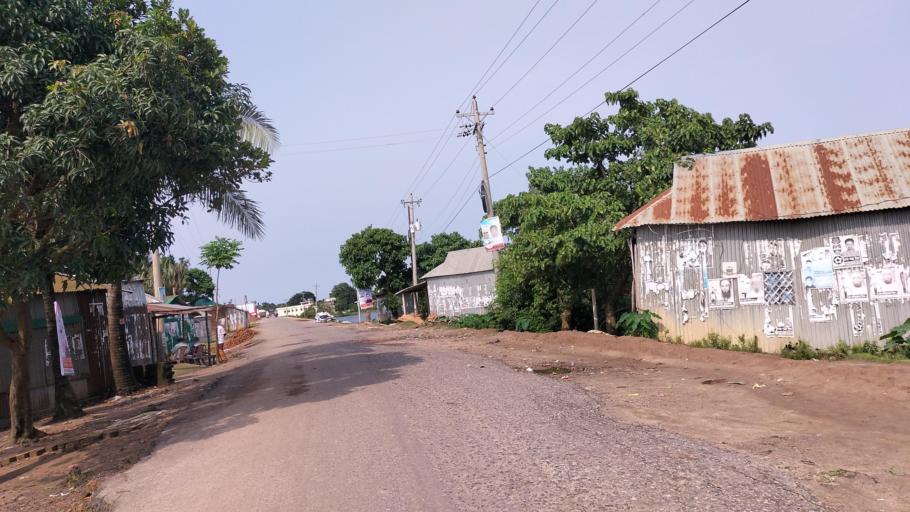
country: BD
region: Dhaka
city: Netrakona
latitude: 25.0723
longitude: 90.8895
